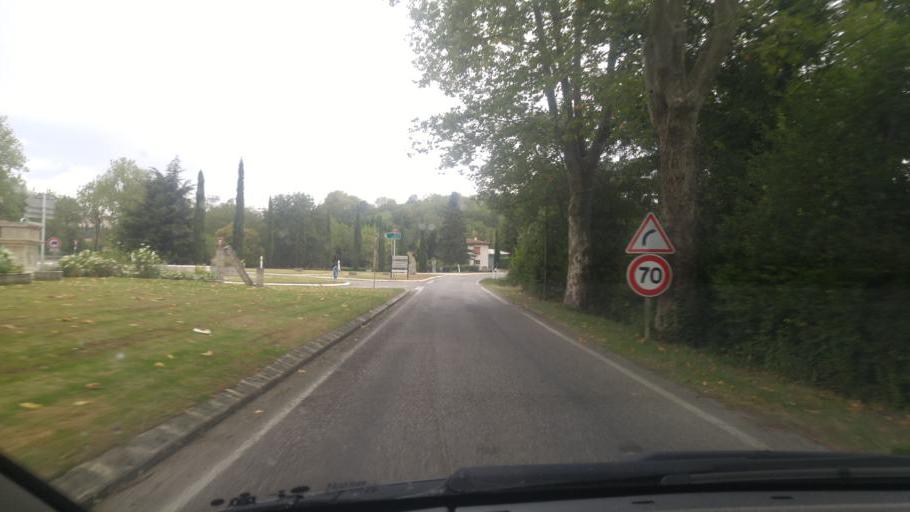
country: FR
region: Midi-Pyrenees
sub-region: Departement du Gers
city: Lectoure
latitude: 43.9247
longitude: 0.6240
